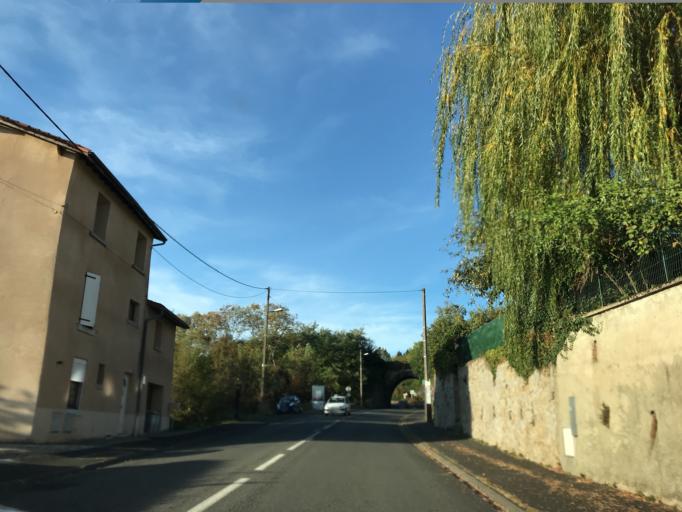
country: FR
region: Auvergne
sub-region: Departement du Puy-de-Dome
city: Thiers
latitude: 45.8627
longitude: 3.5345
